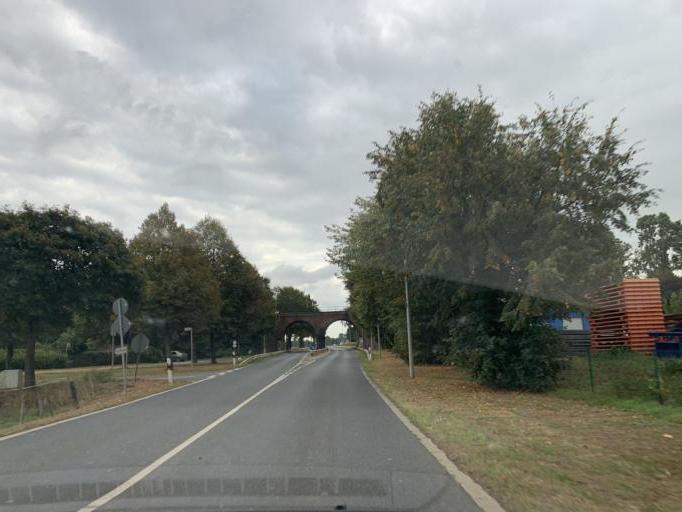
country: DE
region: North Rhine-Westphalia
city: Huckelhoven
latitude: 51.0132
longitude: 6.2374
